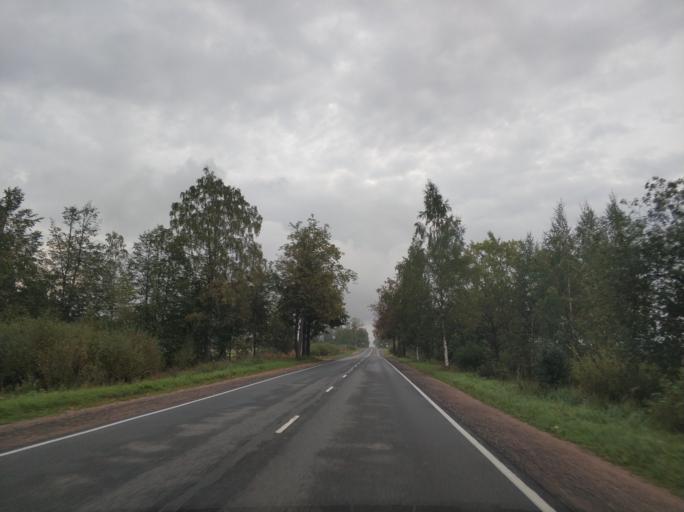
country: RU
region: Leningrad
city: Borisova Griva
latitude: 60.0831
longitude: 30.9023
